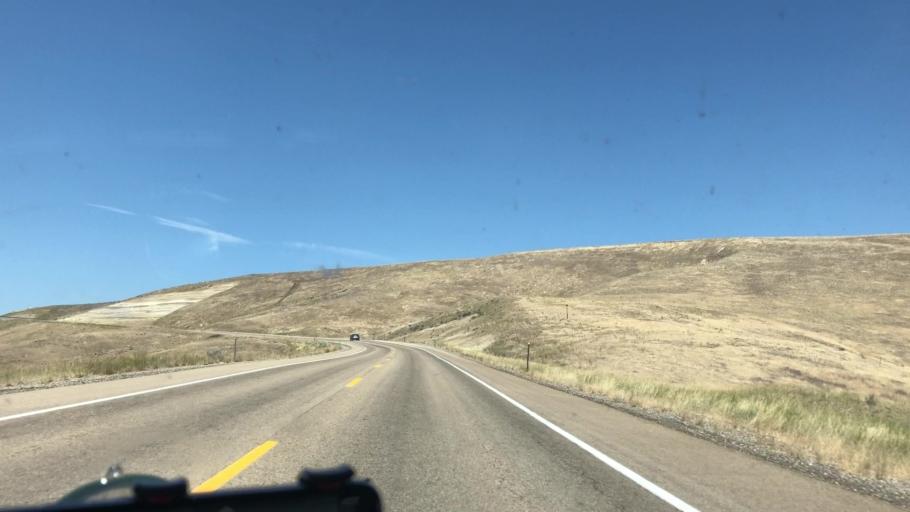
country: US
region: Idaho
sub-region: Owyhee County
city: Marsing
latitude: 43.2853
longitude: -116.9881
